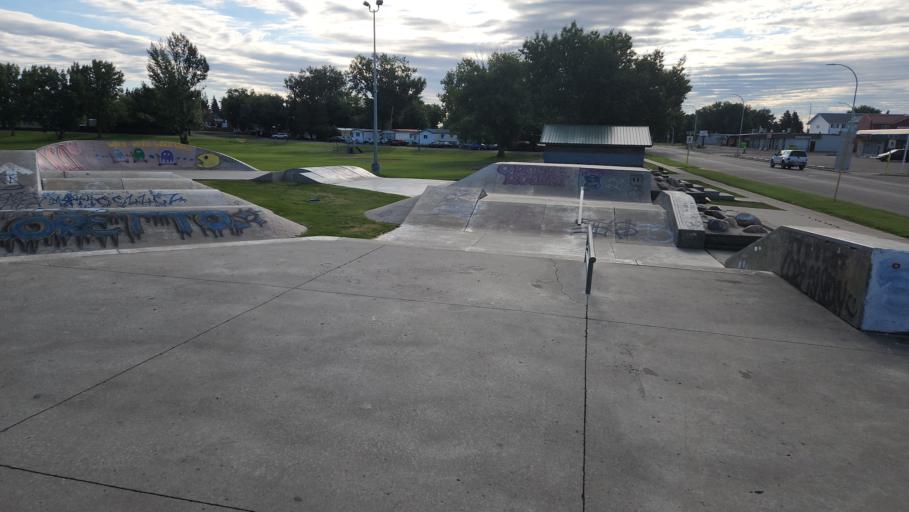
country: CA
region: Alberta
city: Brooks
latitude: 50.5667
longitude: -111.8819
